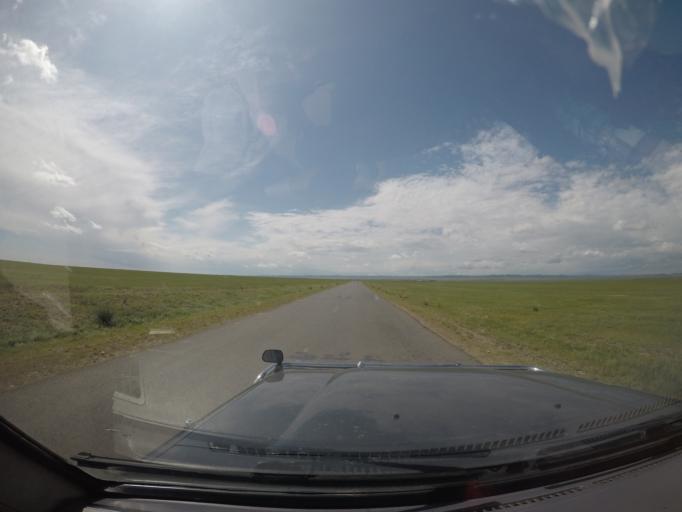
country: MN
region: Hentiy
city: Moron
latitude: 47.4221
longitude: 110.1056
